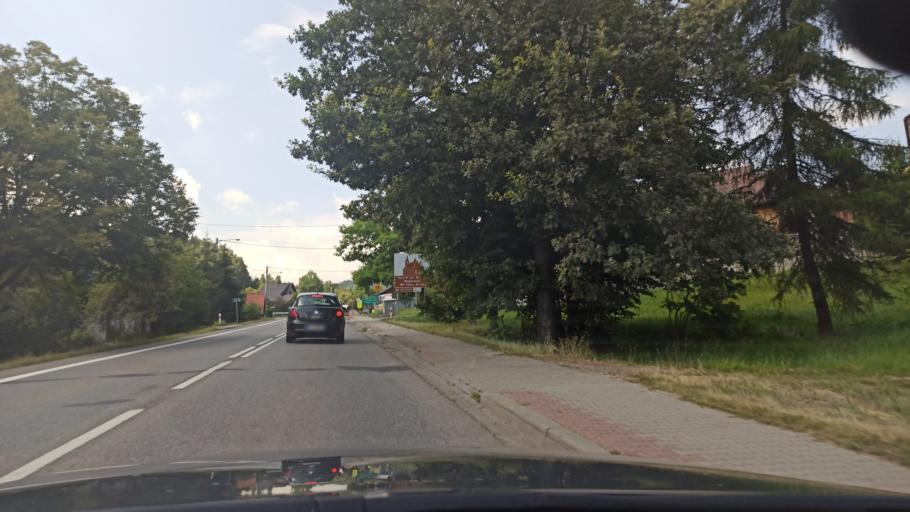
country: PL
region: Lesser Poland Voivodeship
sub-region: Powiat nowotarski
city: Krosnica
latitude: 49.4462
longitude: 20.3423
